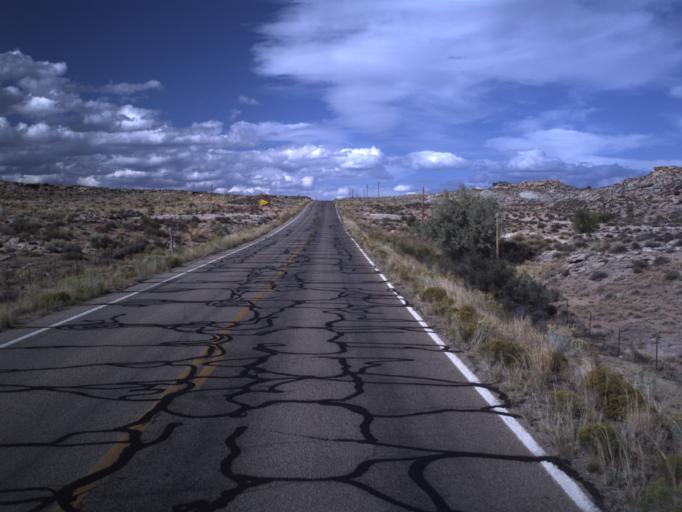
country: US
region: Utah
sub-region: San Juan County
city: Blanding
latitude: 37.2709
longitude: -109.3004
